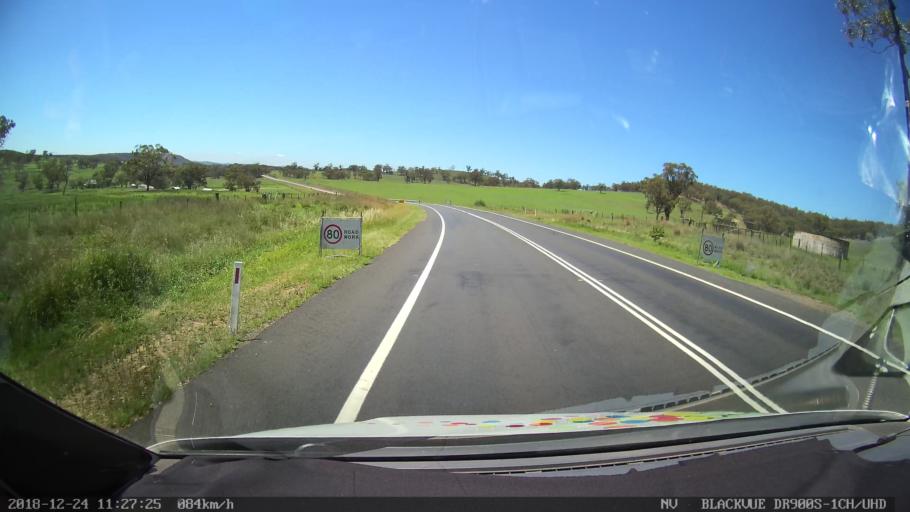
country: AU
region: New South Wales
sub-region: Upper Hunter Shire
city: Merriwa
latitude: -32.1817
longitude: 150.4350
